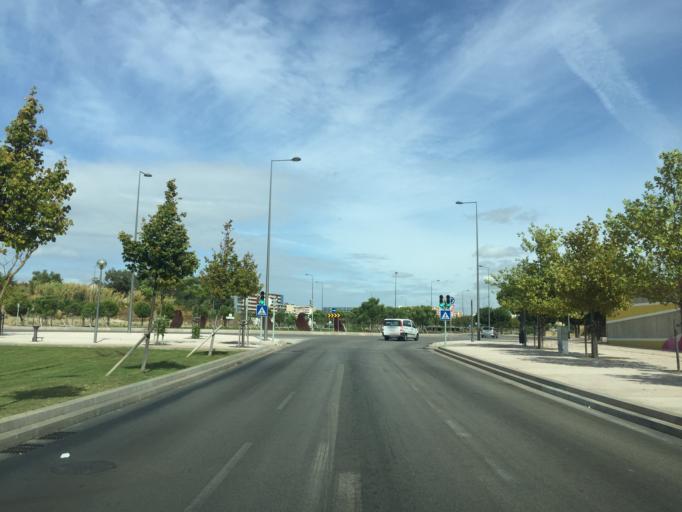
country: PT
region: Lisbon
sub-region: Odivelas
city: Olival do Basto
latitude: 38.7717
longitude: -9.1489
